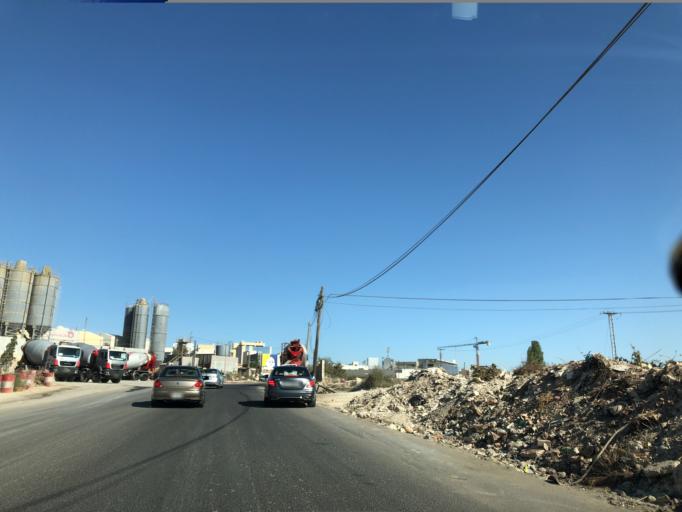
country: JO
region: Amman
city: Wadi as Sir
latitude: 31.9379
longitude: 35.8490
